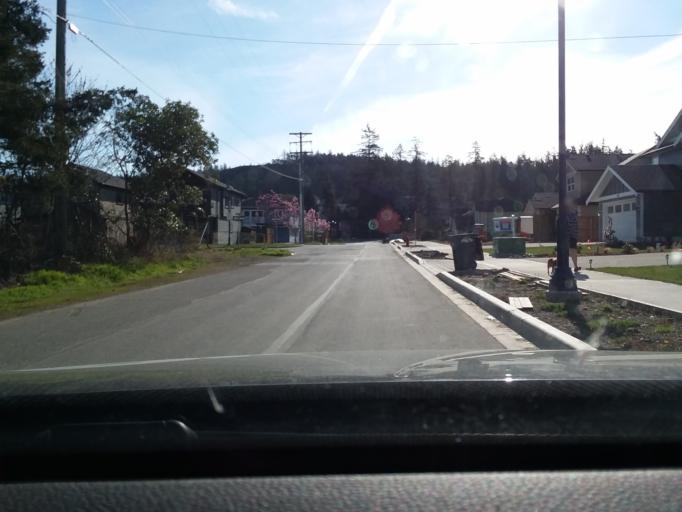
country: CA
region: British Columbia
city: Langford
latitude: 48.4256
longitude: -123.5355
